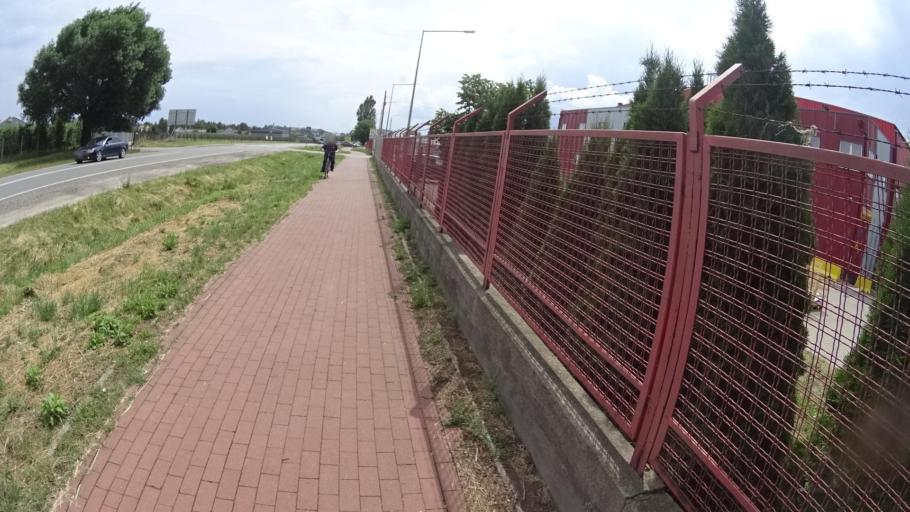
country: PL
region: Masovian Voivodeship
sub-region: Powiat grojecki
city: Grojec
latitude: 51.8823
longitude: 20.8634
